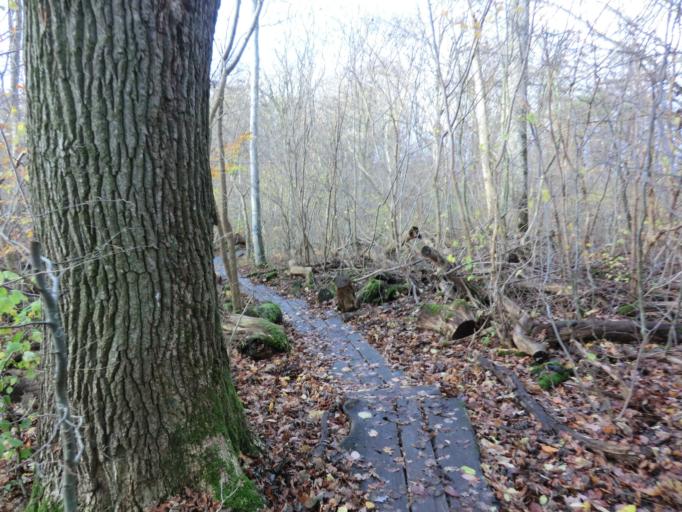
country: SE
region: Skane
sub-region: Lunds Kommun
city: Genarp
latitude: 55.6749
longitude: 13.3354
